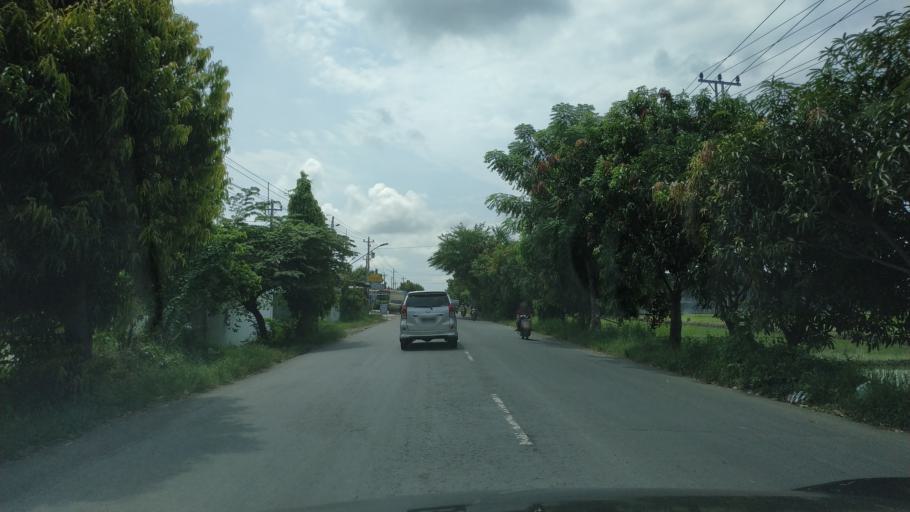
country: ID
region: Central Java
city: Adiwerna
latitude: -6.9276
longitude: 109.1257
